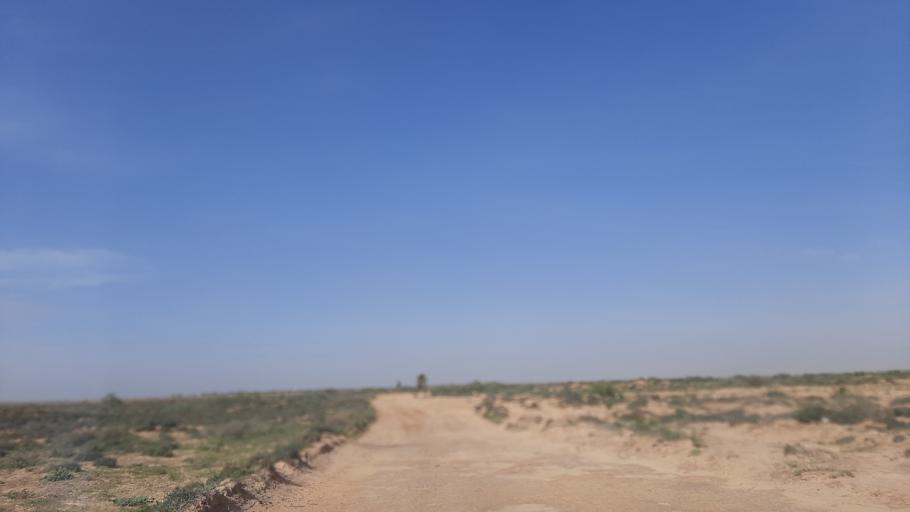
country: TN
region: Madanin
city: Zarzis
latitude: 33.4437
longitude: 10.8085
